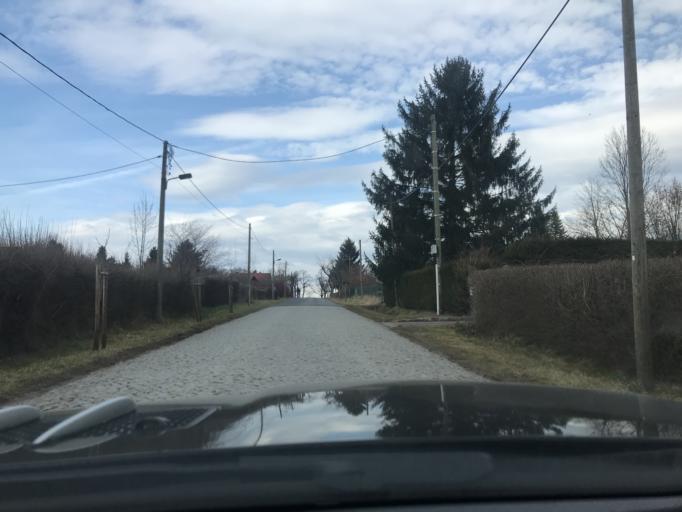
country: DE
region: Thuringia
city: Muehlhausen
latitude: 51.2031
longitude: 10.4187
